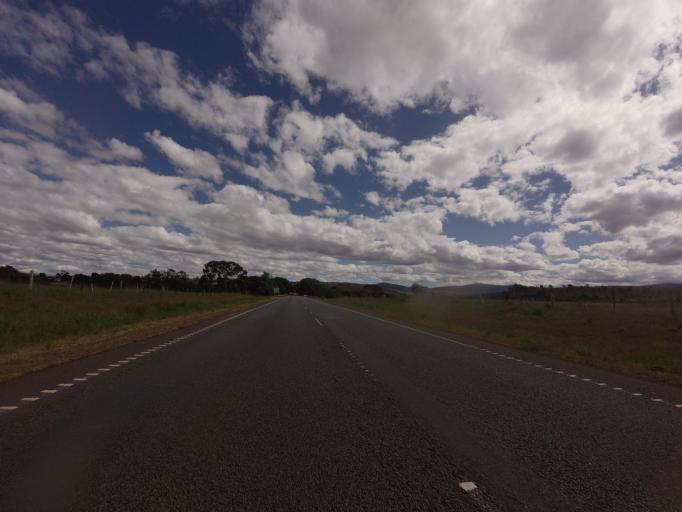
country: AU
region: Tasmania
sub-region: Northern Midlands
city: Evandale
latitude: -42.1363
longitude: 147.4233
